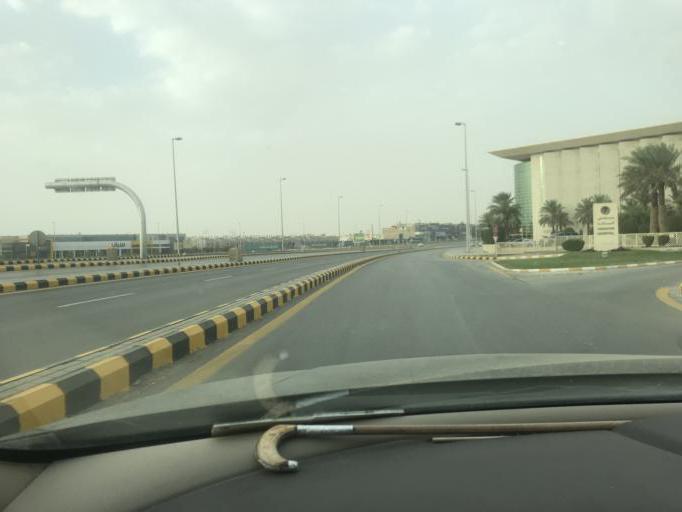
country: SA
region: Ar Riyad
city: Riyadh
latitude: 24.8009
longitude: 46.6533
